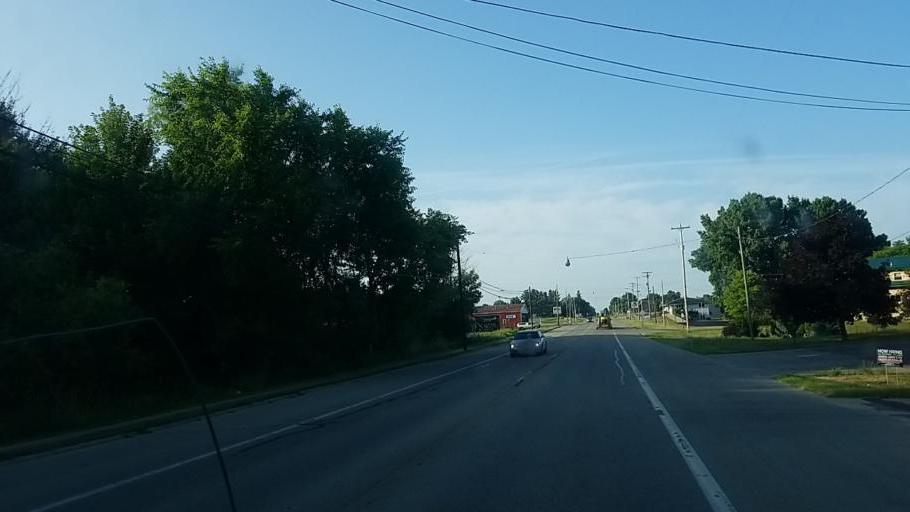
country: US
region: Michigan
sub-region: Montcalm County
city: Stanton
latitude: 43.2089
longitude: -85.0737
